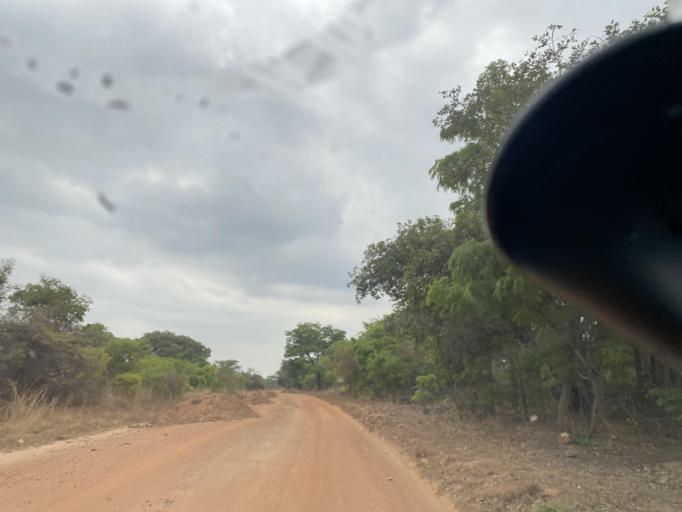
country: ZM
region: Lusaka
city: Chongwe
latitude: -15.2431
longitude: 28.7230
